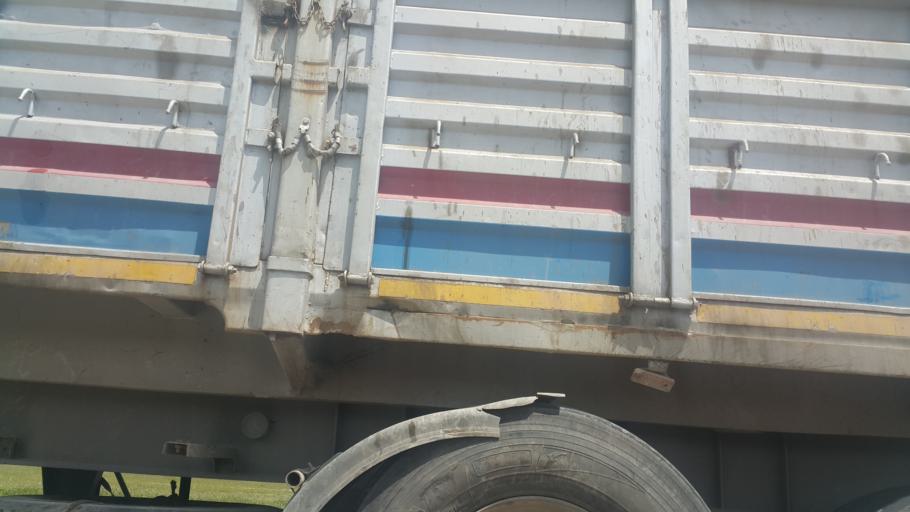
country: TR
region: Osmaniye
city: Toprakkale
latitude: 37.0566
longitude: 36.1222
